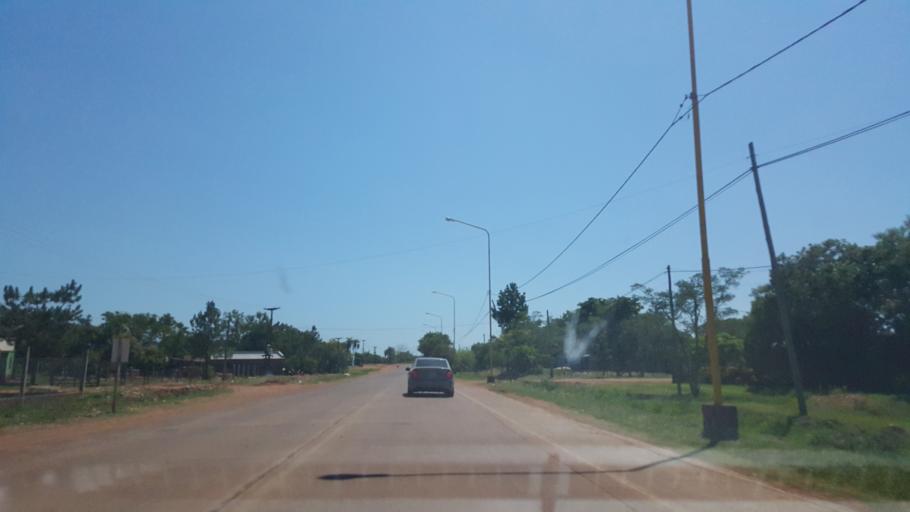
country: AR
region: Corrientes
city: Santo Tome
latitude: -28.5488
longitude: -56.0642
